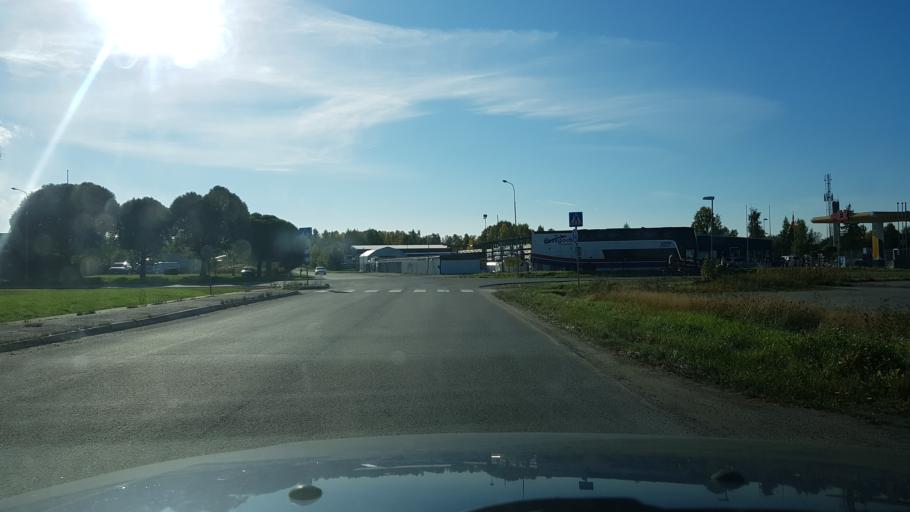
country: SE
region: Norrbotten
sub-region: Pitea Kommun
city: Bergsviken
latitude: 65.3412
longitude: 21.4096
